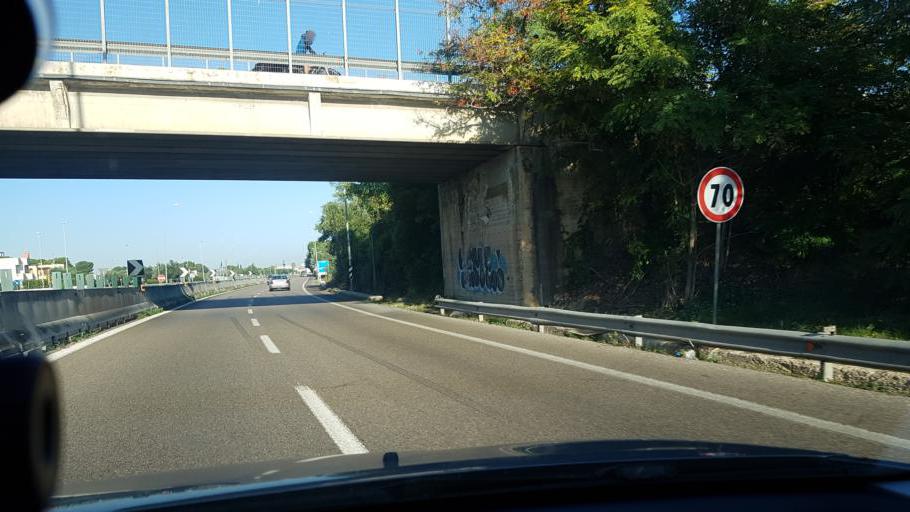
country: IT
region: Apulia
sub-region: Provincia di Bari
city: Parco Scizzo-Parchitello
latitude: 41.0844
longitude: 16.9937
